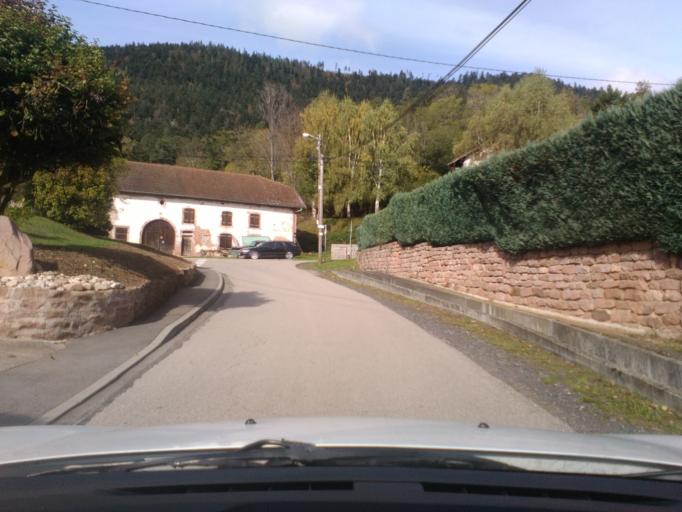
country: FR
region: Lorraine
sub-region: Departement des Vosges
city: Sainte-Marguerite
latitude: 48.2977
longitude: 7.0080
